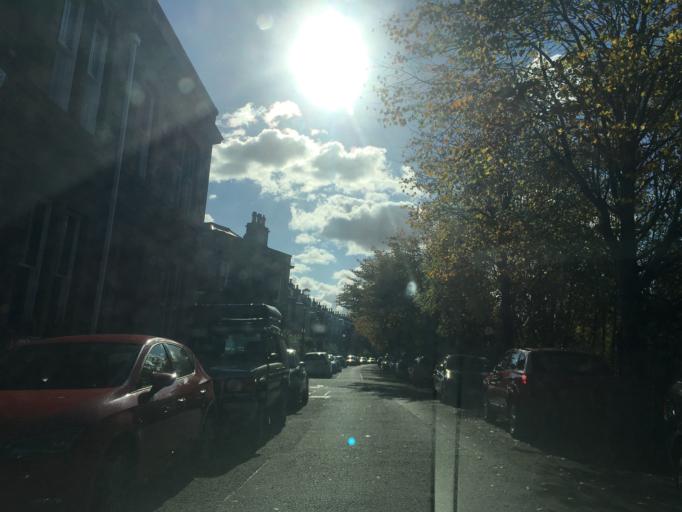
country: GB
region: Scotland
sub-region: Edinburgh
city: Colinton
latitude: 55.9337
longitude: -3.2324
